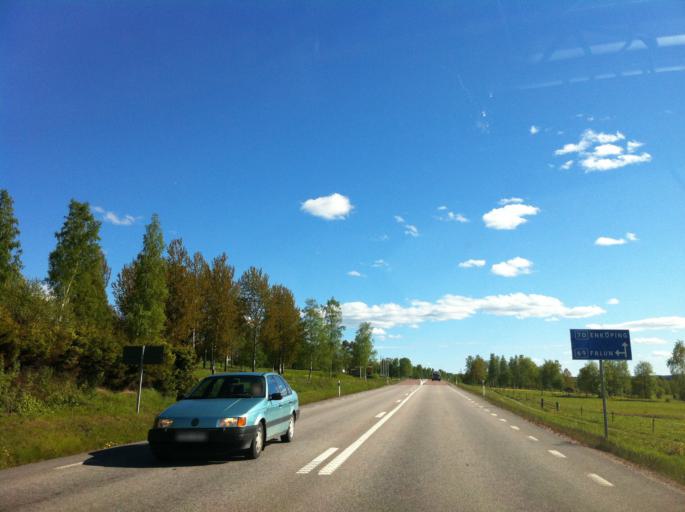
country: SE
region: Dalarna
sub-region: Rattviks Kommun
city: Raettvik
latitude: 60.8716
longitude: 15.1022
